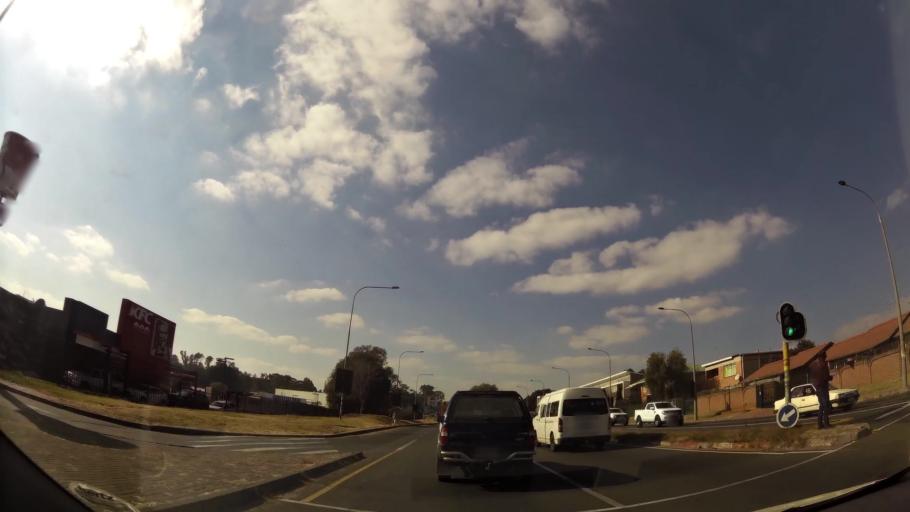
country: ZA
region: Gauteng
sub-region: West Rand District Municipality
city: Krugersdorp
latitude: -26.0892
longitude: 27.7825
